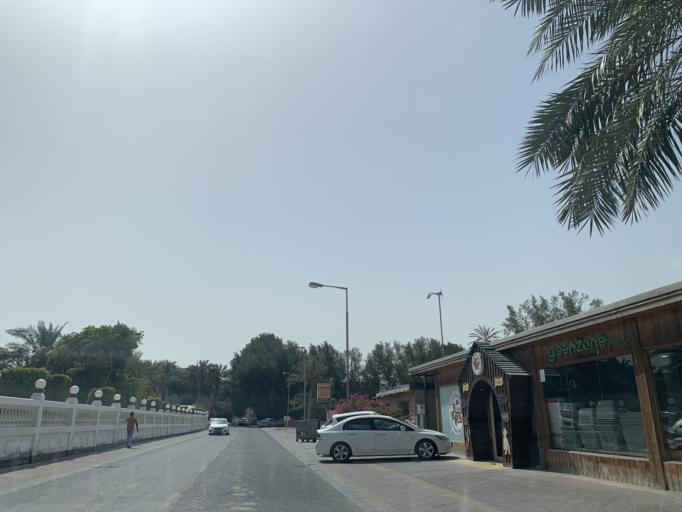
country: BH
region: Manama
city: Jidd Hafs
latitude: 26.2209
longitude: 50.5590
